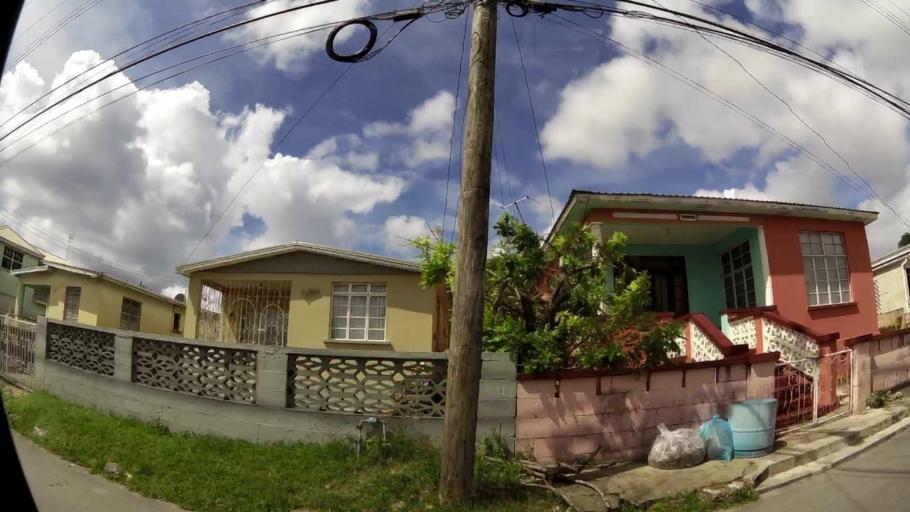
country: BB
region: Saint Michael
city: Bridgetown
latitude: 13.1247
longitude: -59.6179
